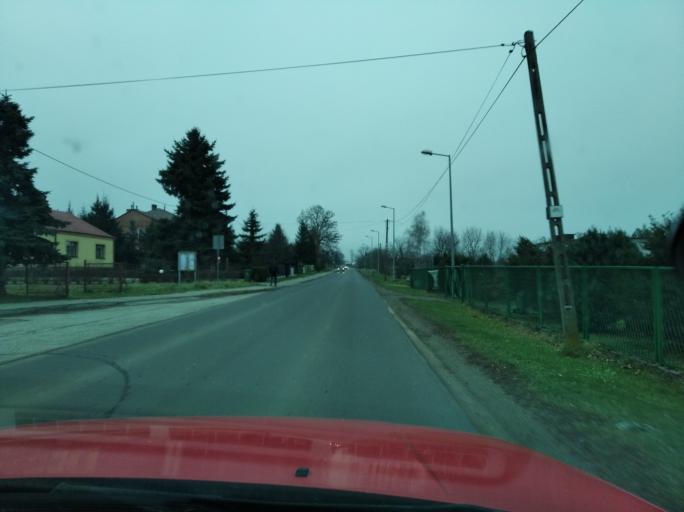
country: PL
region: Subcarpathian Voivodeship
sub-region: Powiat jaroslawski
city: Pawlosiow
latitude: 50.0119
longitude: 22.6494
